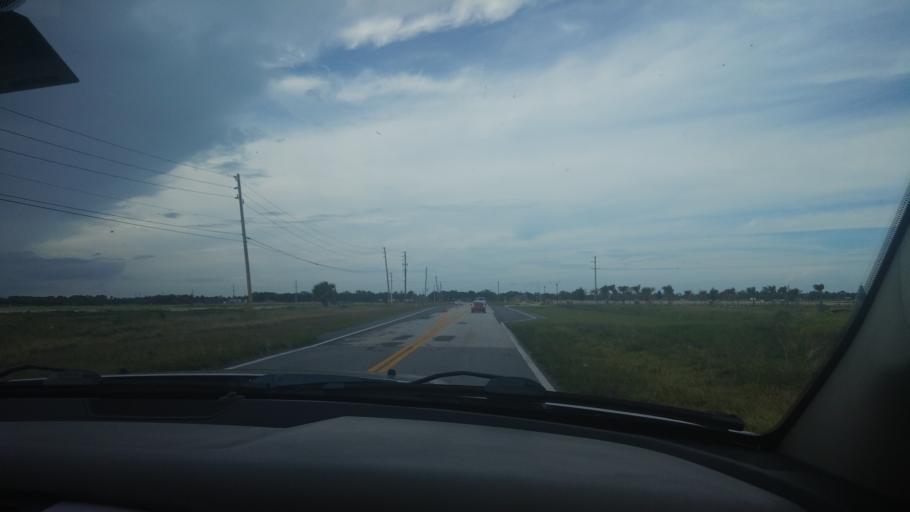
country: US
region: Florida
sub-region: Brevard County
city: Grant-Valkaria
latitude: 27.8988
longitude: -80.6223
